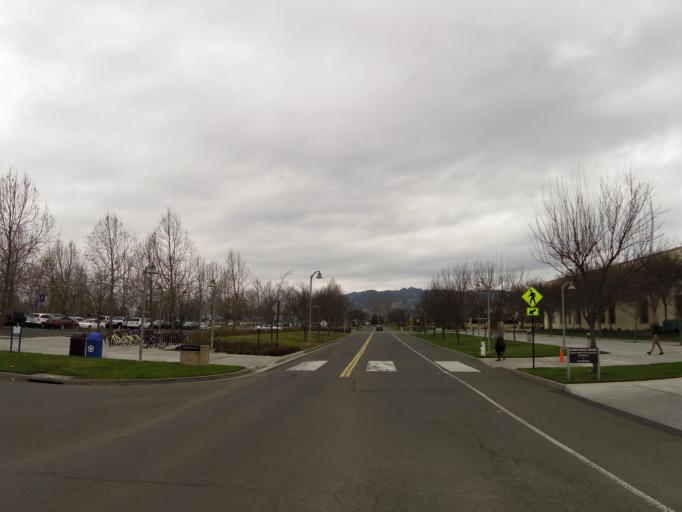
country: US
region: California
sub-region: Sonoma County
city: Rohnert Park
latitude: 38.3434
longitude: -122.6704
